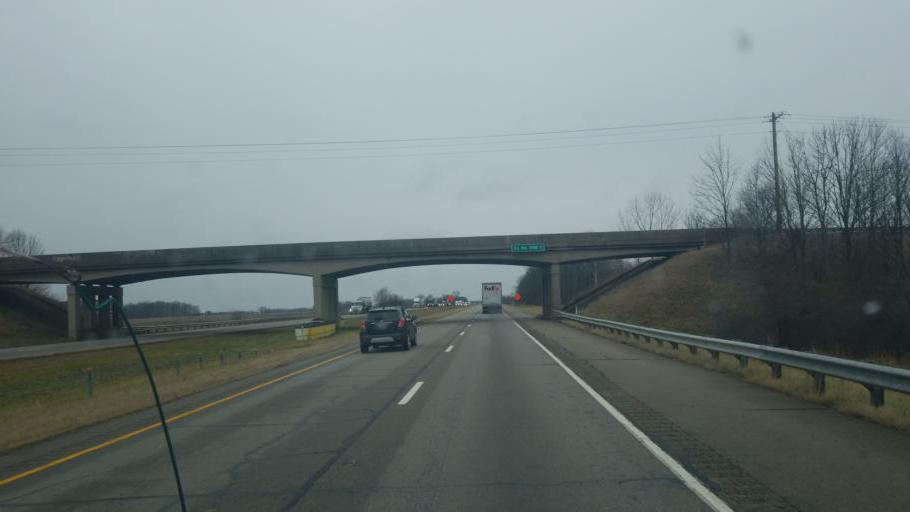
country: US
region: Indiana
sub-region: Henry County
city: New Castle
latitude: 39.8531
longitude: -85.3097
